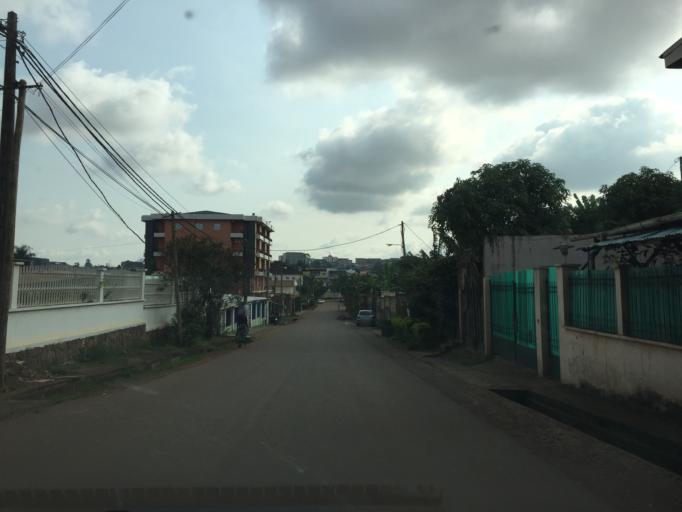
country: CM
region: Centre
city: Yaounde
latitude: 3.8840
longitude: 11.5164
